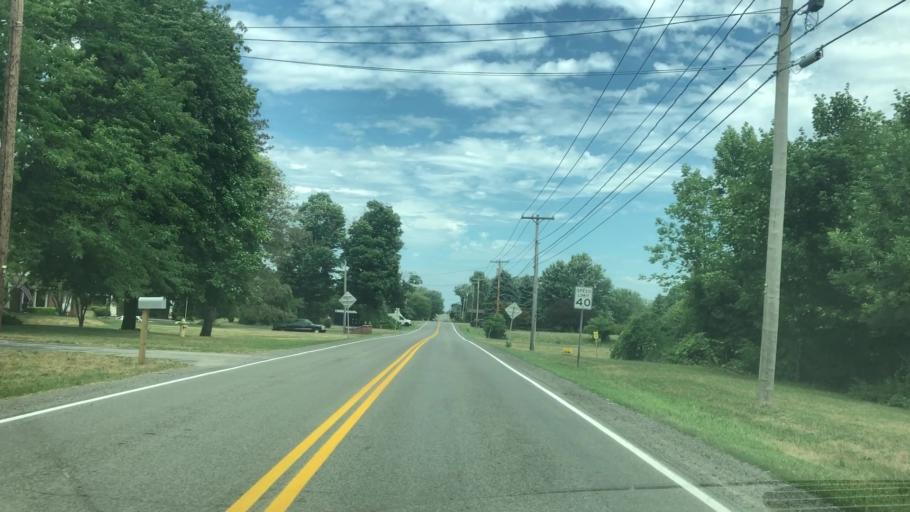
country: US
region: New York
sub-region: Monroe County
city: Webster
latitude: 43.1608
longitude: -77.4005
